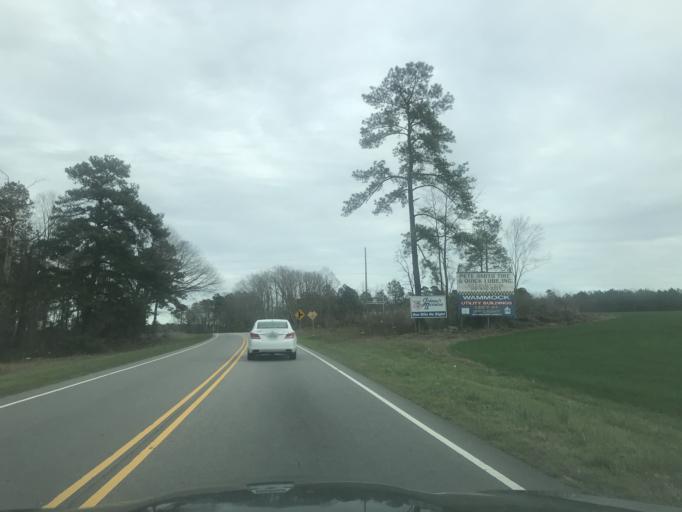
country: US
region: North Carolina
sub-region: Franklin County
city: Louisburg
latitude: 36.0823
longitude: -78.3418
